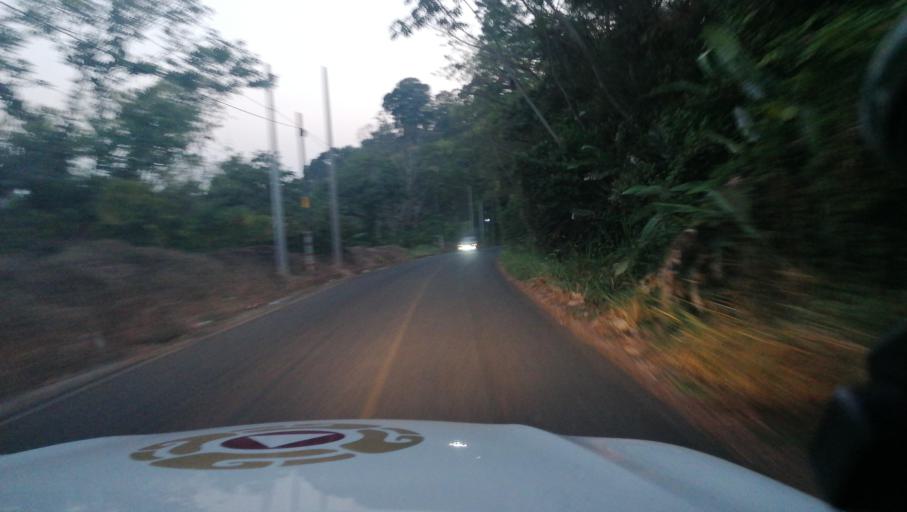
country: MX
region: Chiapas
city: Veinte de Noviembre
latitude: 15.0018
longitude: -92.2434
